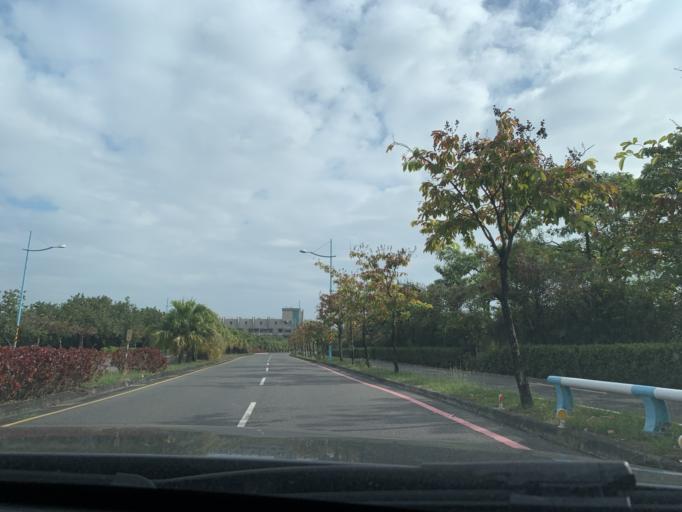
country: TW
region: Taiwan
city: Fengshan
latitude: 22.4541
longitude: 120.4862
